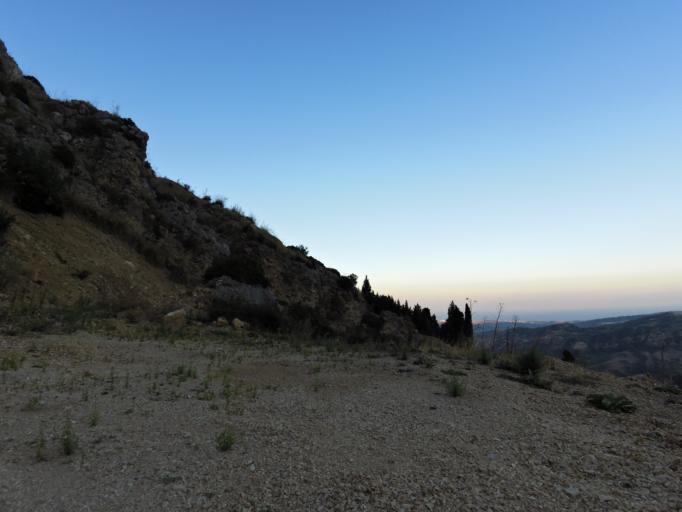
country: IT
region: Calabria
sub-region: Provincia di Reggio Calabria
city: Pazzano
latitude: 38.4746
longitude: 16.4592
